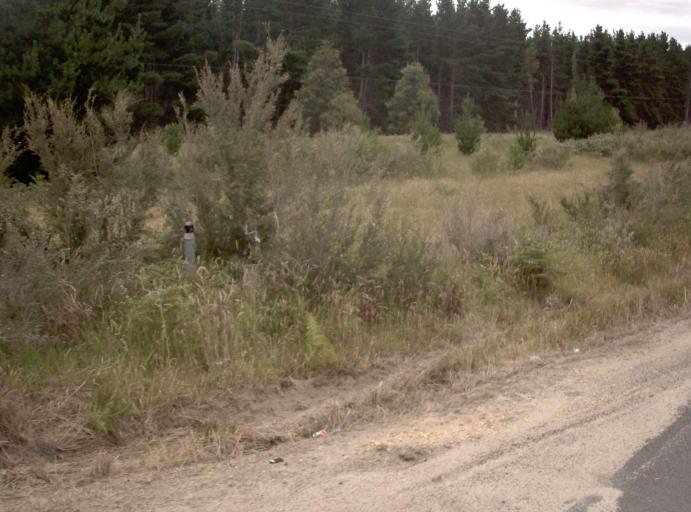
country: AU
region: Victoria
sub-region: Wellington
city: Sale
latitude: -38.2196
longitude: 147.0590
